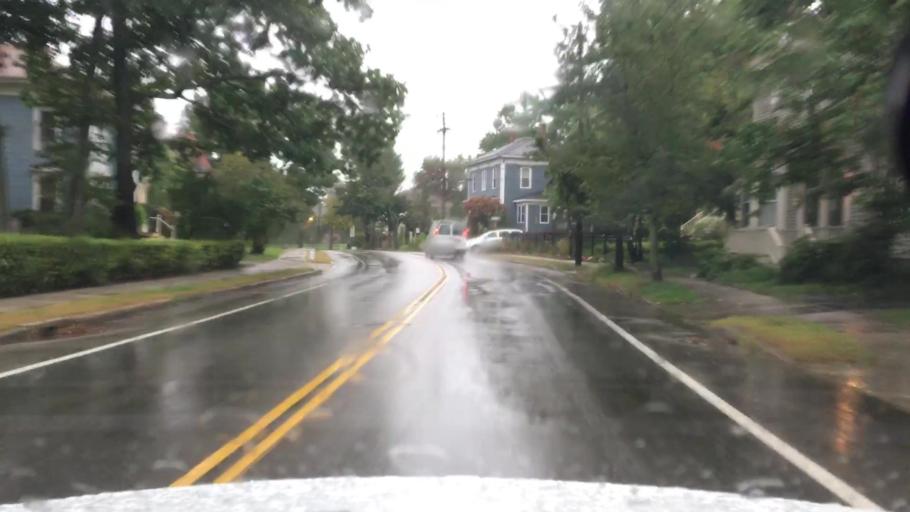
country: US
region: Maine
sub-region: Cumberland County
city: Portland
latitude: 43.6682
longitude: -70.2841
